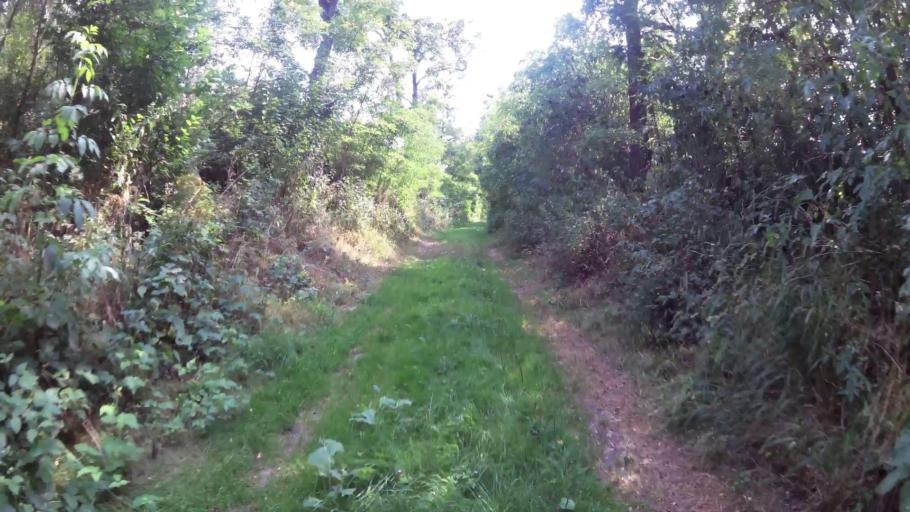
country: PL
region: West Pomeranian Voivodeship
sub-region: Powiat gryfinski
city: Chojna
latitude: 52.9066
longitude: 14.5068
